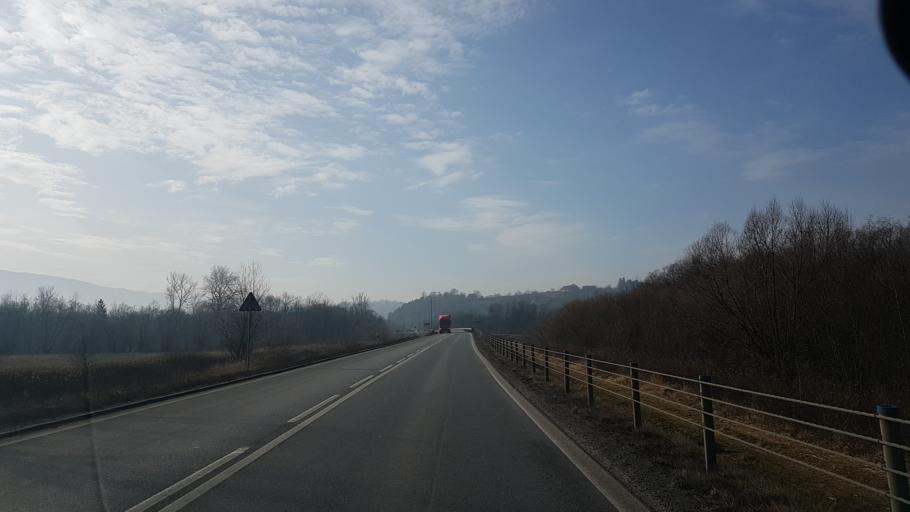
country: PL
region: Lesser Poland Voivodeship
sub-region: Powiat nowosadecki
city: Podegrodzie
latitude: 49.5608
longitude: 20.5820
